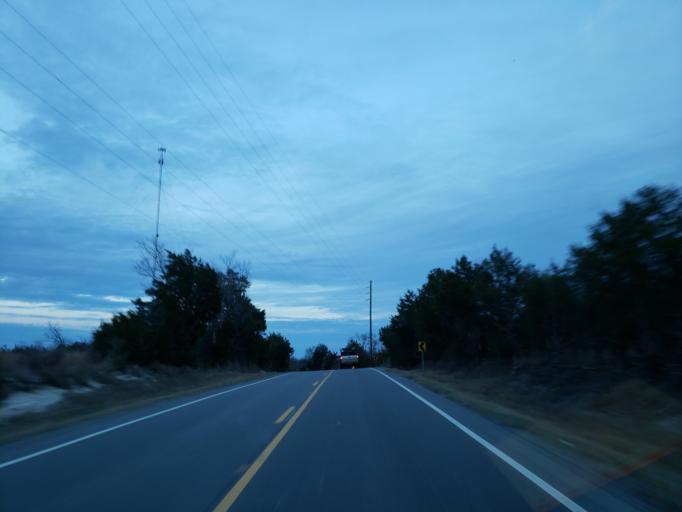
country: US
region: Alabama
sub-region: Sumter County
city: Livingston
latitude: 32.8072
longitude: -88.2946
